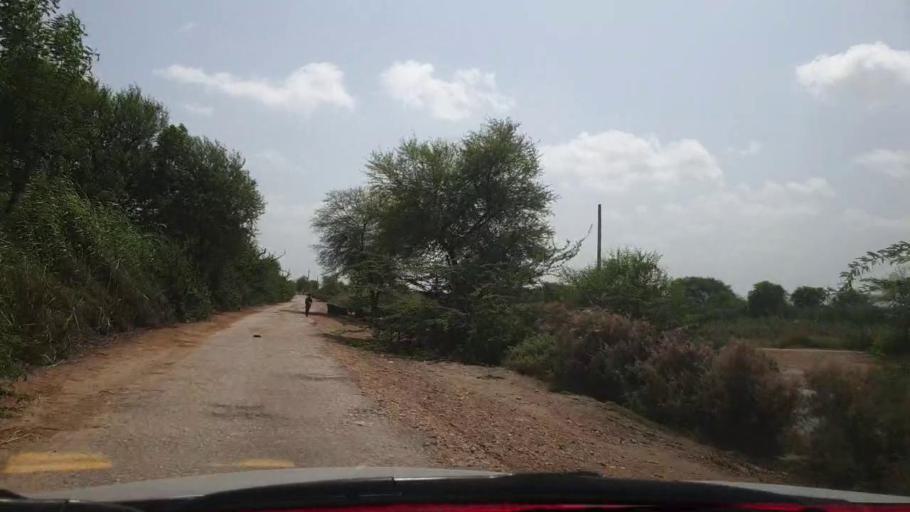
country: PK
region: Sindh
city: Talhar
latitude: 24.8923
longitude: 68.9063
